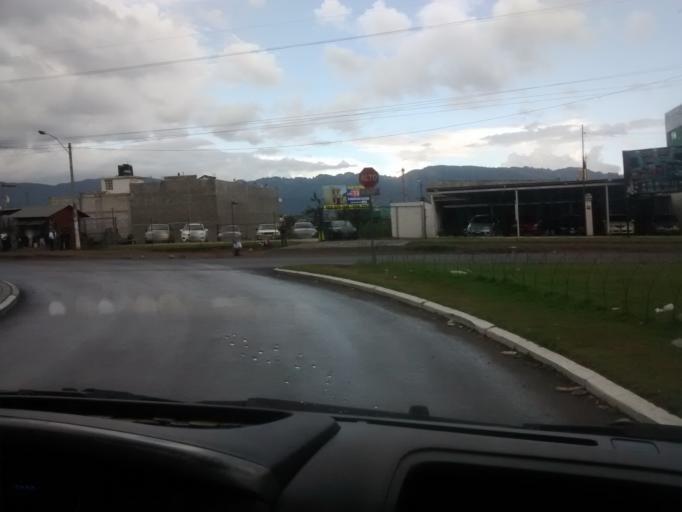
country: GT
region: Quetzaltenango
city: Olintepeque
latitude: 14.8593
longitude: -91.5209
